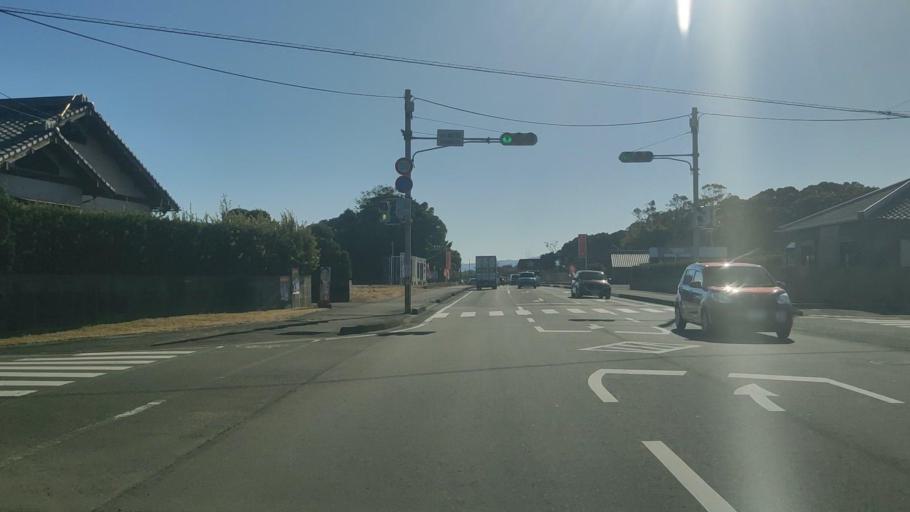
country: JP
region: Miyazaki
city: Miyazaki-shi
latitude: 31.9514
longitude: 131.4603
